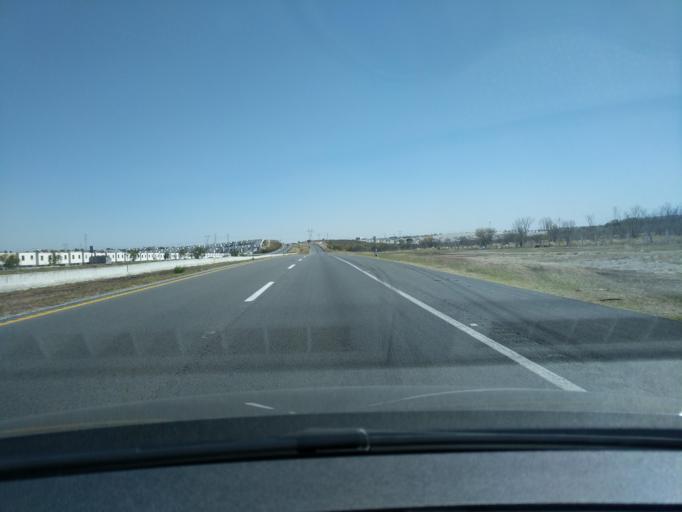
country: MX
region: Nuevo Leon
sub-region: Apodaca
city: Loma la Paz
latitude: 25.7088
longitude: -100.1081
